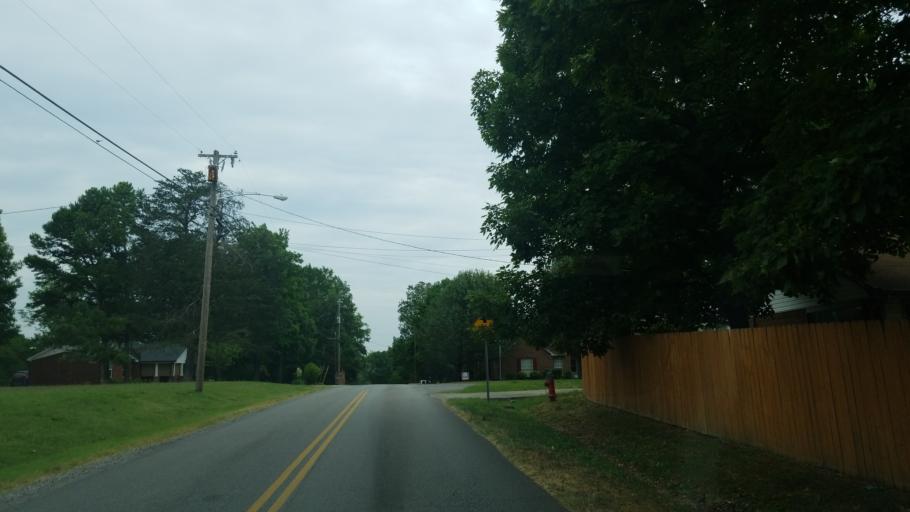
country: US
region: Tennessee
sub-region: Rutherford County
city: La Vergne
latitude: 36.0376
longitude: -86.5884
